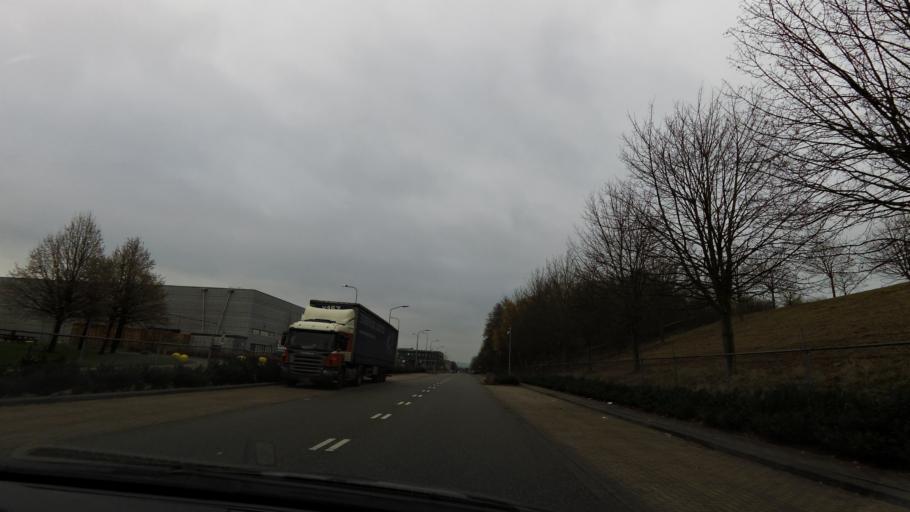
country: NL
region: Limburg
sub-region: Gemeente Simpelveld
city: Simpelveld
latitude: 50.8531
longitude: 5.9981
